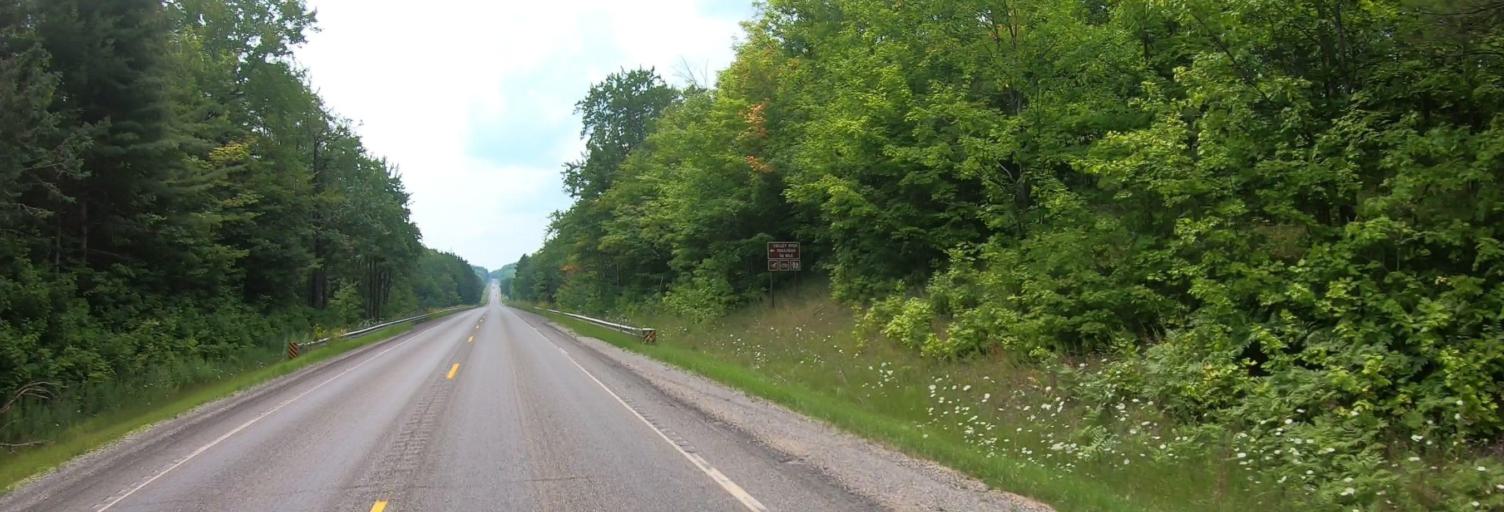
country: US
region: Michigan
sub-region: Alger County
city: Munising
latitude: 46.3676
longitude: -86.7093
